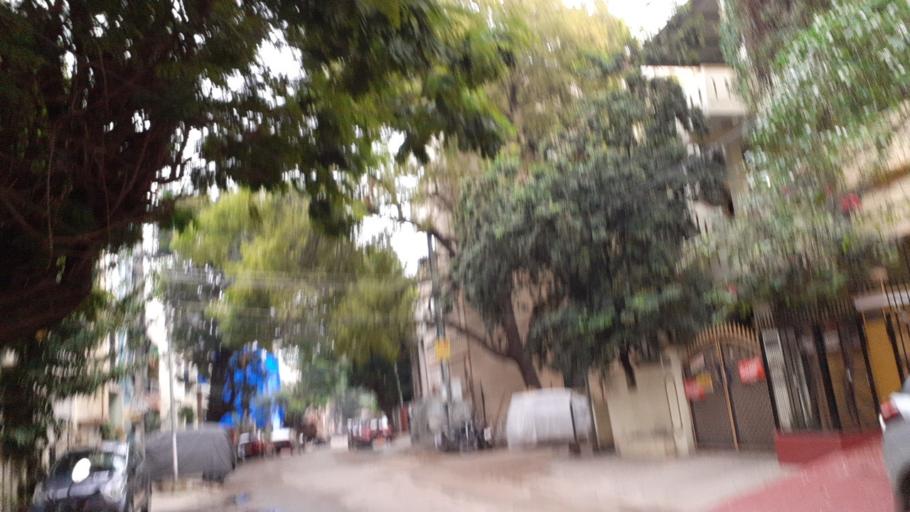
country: IN
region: Telangana
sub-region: Rangareddi
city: Kukatpalli
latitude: 17.4472
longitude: 78.4458
